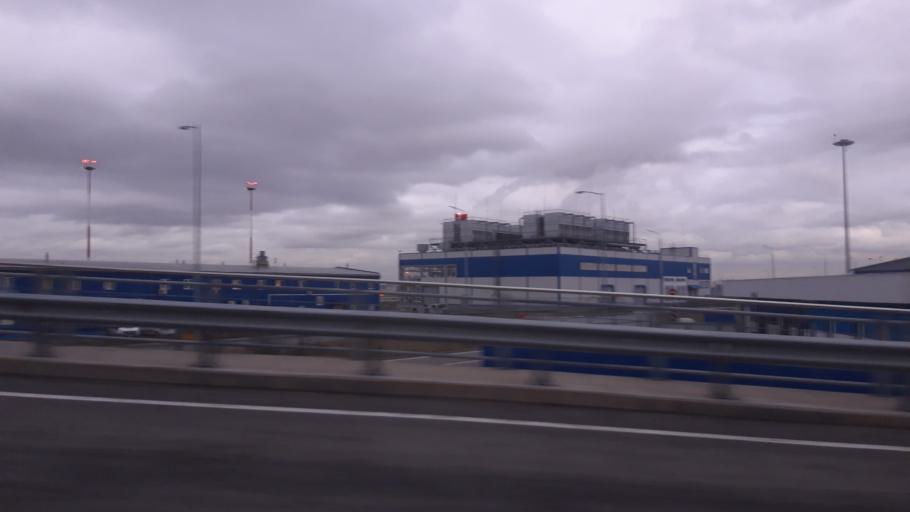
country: RU
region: St.-Petersburg
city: Dachnoye
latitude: 59.7998
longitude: 30.2783
